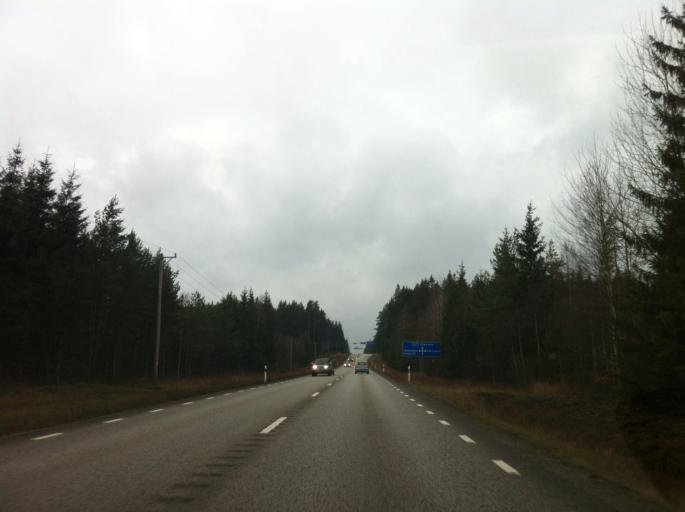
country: SE
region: Joenkoeping
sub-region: Vetlanda Kommun
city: Vetlanda
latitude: 57.4157
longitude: 15.0232
